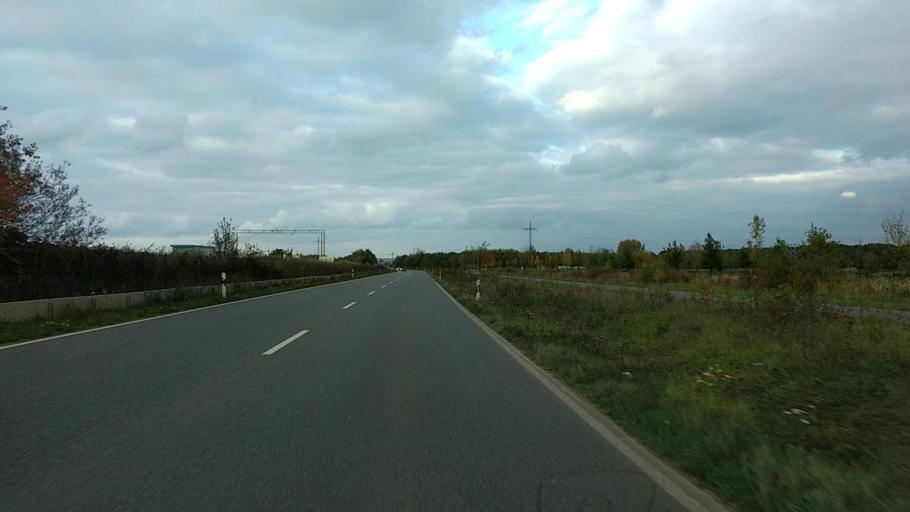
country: DE
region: North Rhine-Westphalia
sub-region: Regierungsbezirk Koln
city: Kerpen
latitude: 50.8789
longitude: 6.6410
